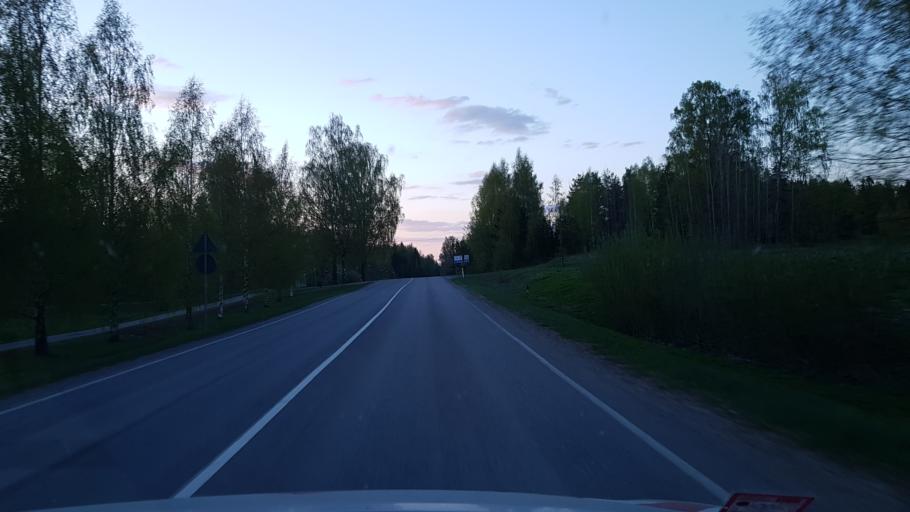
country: EE
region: Vorumaa
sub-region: Voru linn
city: Voru
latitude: 57.7952
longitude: 27.0341
